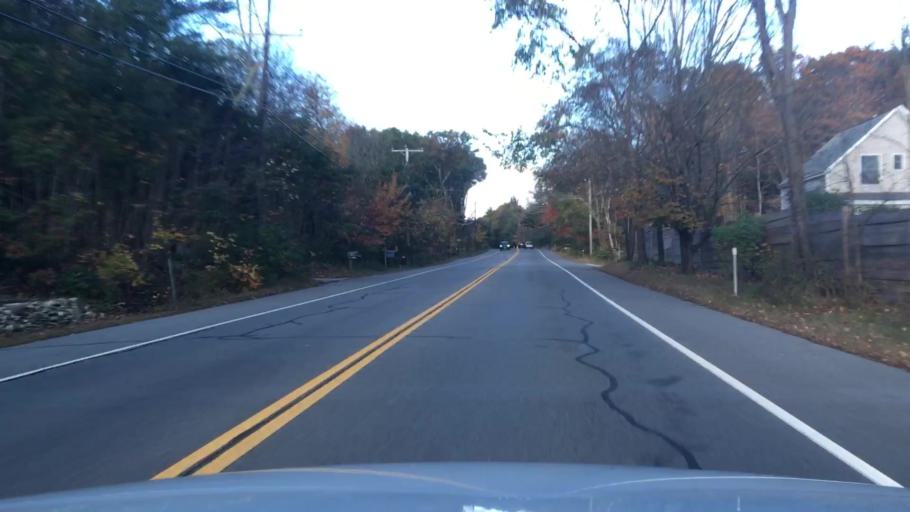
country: US
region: New Hampshire
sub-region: Strafford County
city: Lee
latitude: 43.1514
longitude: -71.0247
